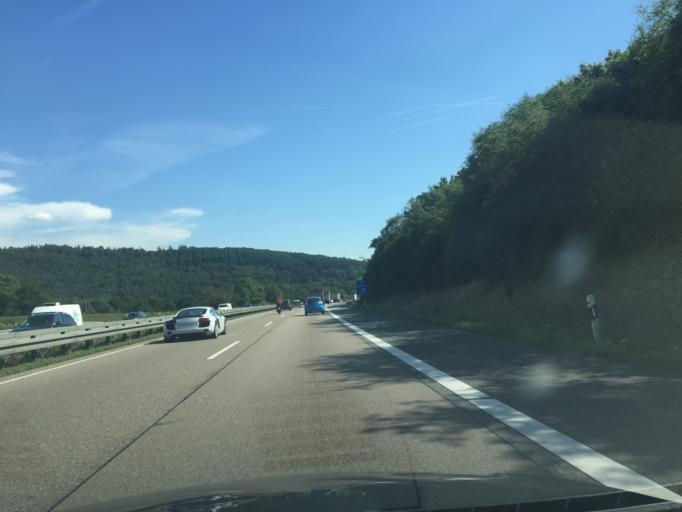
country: DE
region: Hesse
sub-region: Regierungsbezirk Giessen
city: Sinn
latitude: 50.6484
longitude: 8.3230
